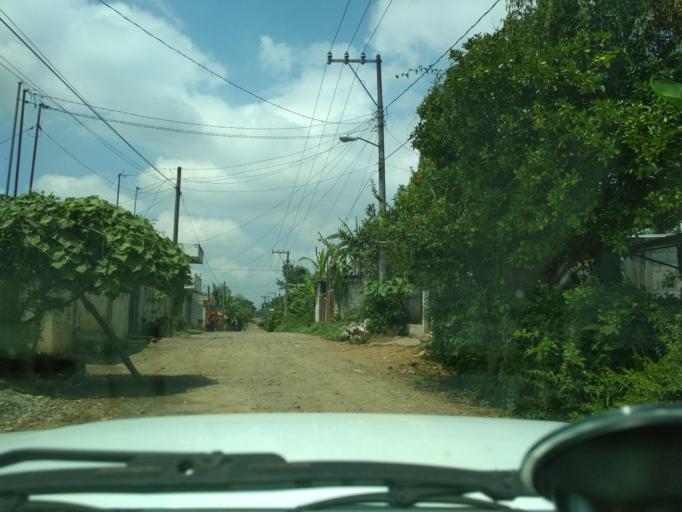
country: MX
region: Veracruz
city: Monte Blanco
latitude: 18.9668
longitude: -97.0128
